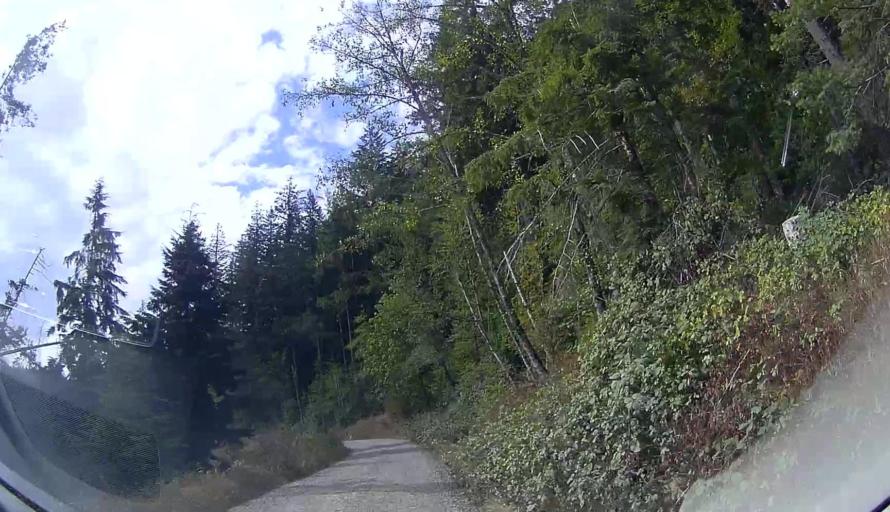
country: US
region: Washington
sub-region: Whatcom County
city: Sudden Valley
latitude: 48.6128
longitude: -122.4181
